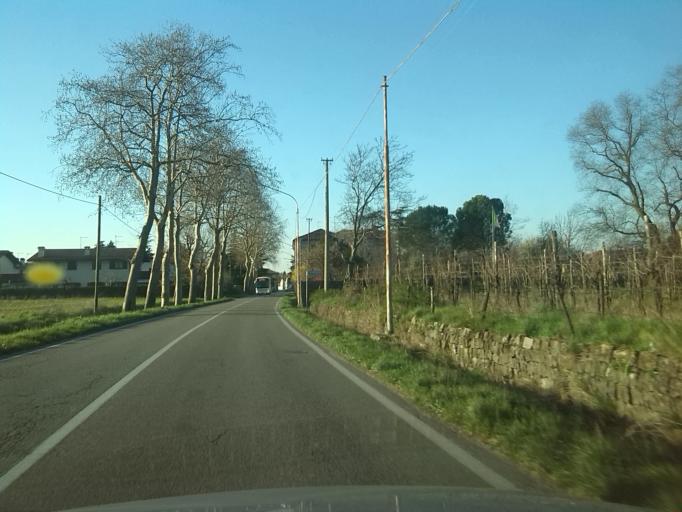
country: IT
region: Friuli Venezia Giulia
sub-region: Provincia di Udine
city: Cividale del Friuli
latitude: 46.0751
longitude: 13.4357
